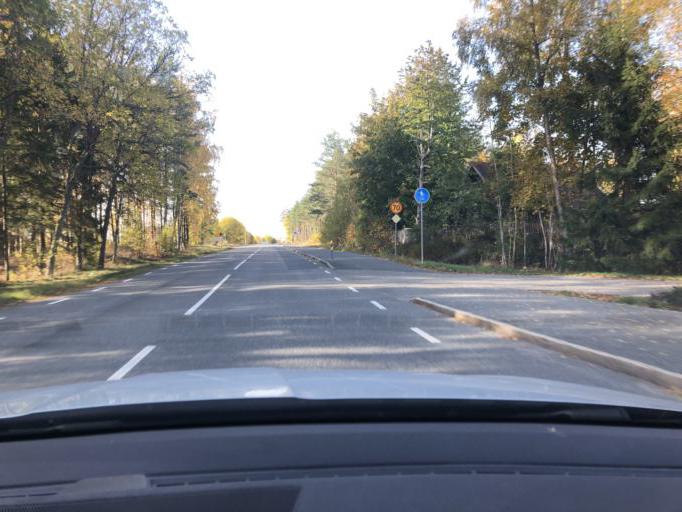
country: SE
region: Joenkoeping
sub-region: Jonkopings Kommun
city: Jonkoping
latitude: 57.7714
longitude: 14.1013
